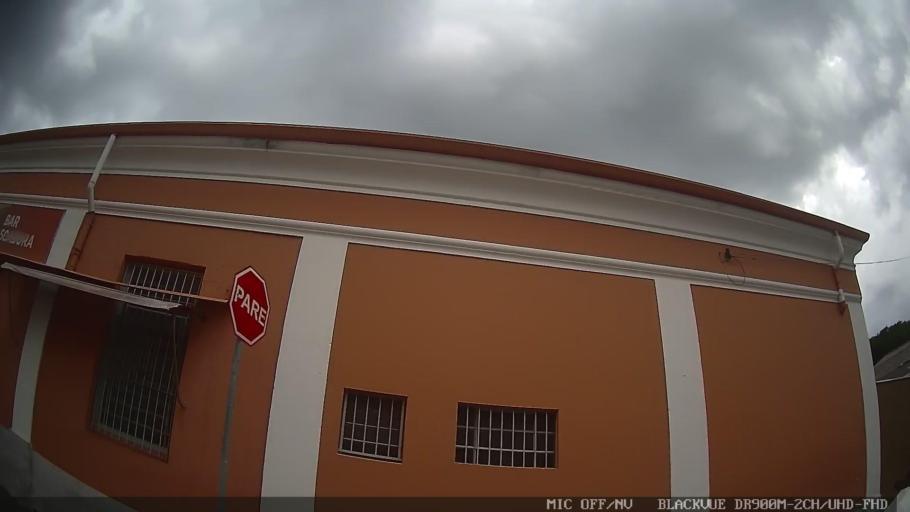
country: BR
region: Sao Paulo
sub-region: Amparo
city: Amparo
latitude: -22.7034
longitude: -46.7560
